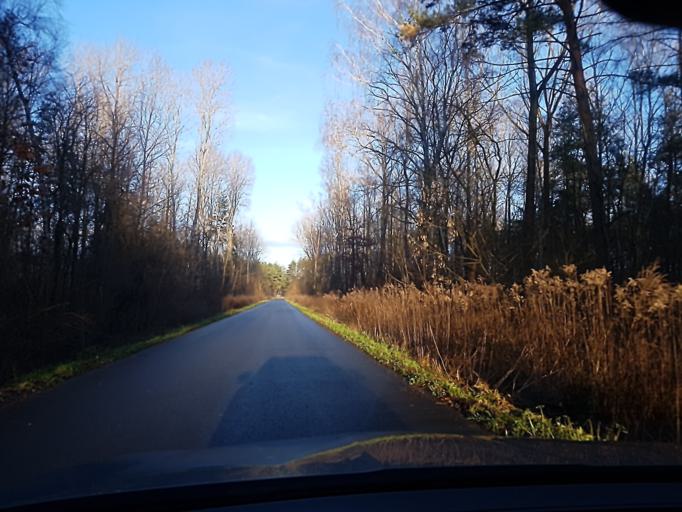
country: DE
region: Brandenburg
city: Trobitz
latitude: 51.5893
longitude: 13.4212
